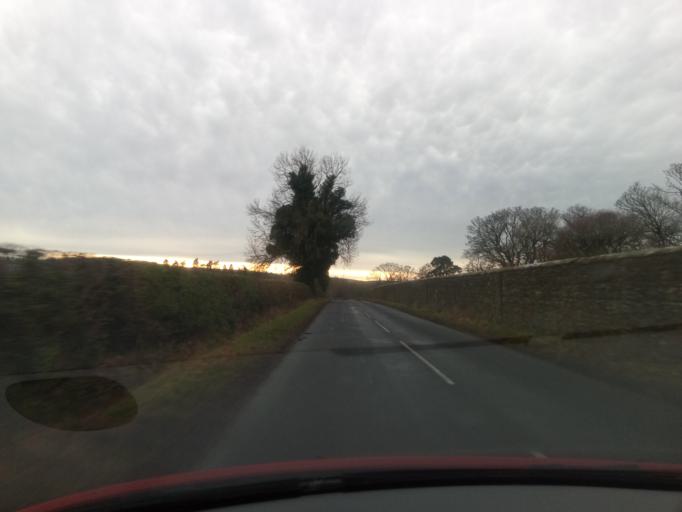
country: GB
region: England
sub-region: Northumberland
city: Alnwick
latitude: 55.4269
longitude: -1.7145
